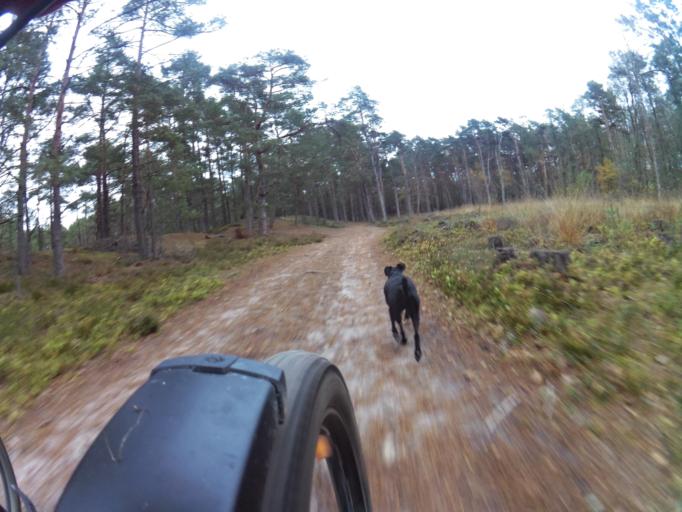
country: PL
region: Pomeranian Voivodeship
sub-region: Powiat leborski
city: Leba
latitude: 54.7786
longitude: 17.7058
